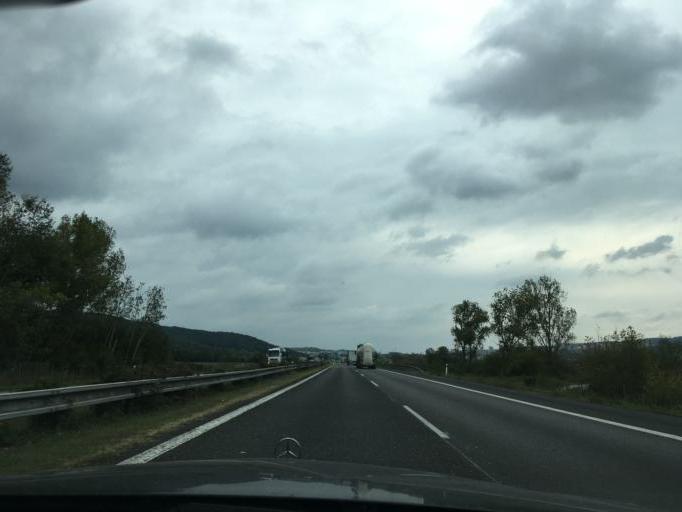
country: SK
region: Bratislavsky
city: Stupava
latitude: 48.2238
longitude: 17.0268
